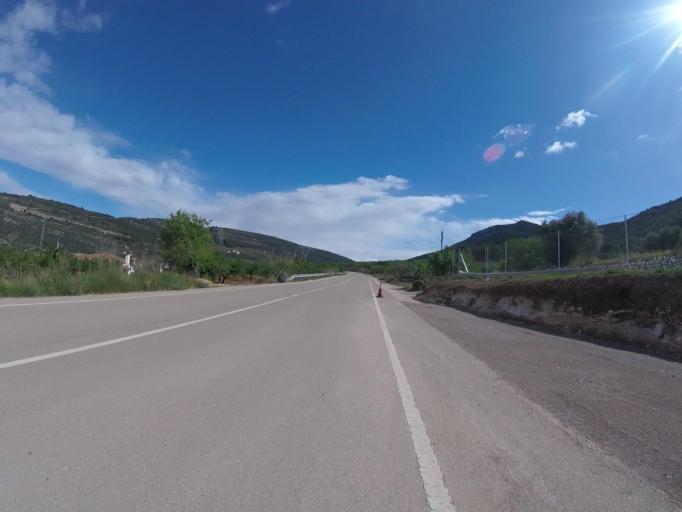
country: ES
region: Valencia
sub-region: Provincia de Castello
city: Culla
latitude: 40.2827
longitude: -0.1118
